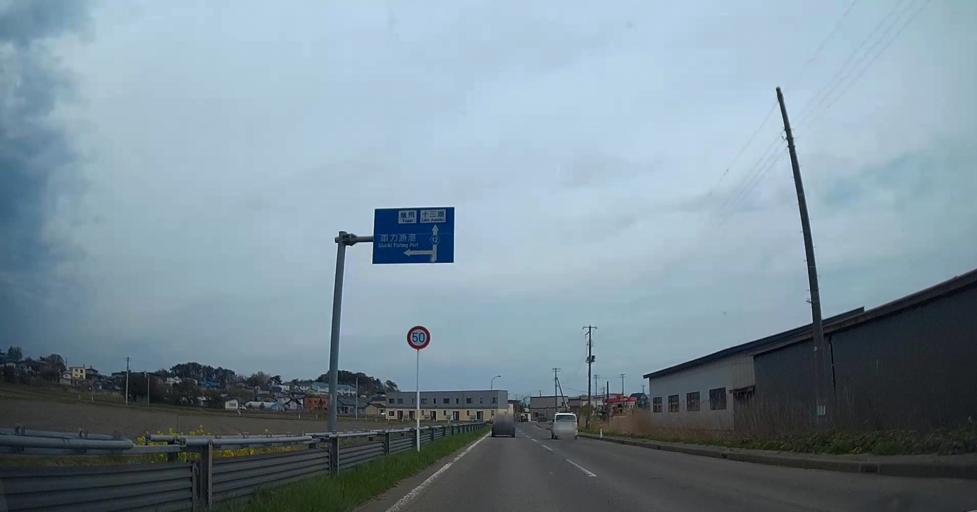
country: JP
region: Aomori
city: Shimokizukuri
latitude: 40.9763
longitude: 140.3699
